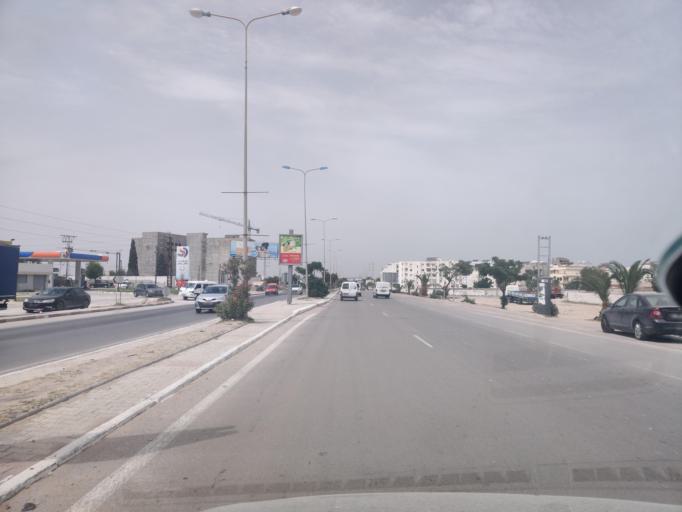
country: TN
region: Susah
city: Hammam Sousse
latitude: 35.8353
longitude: 10.5881
